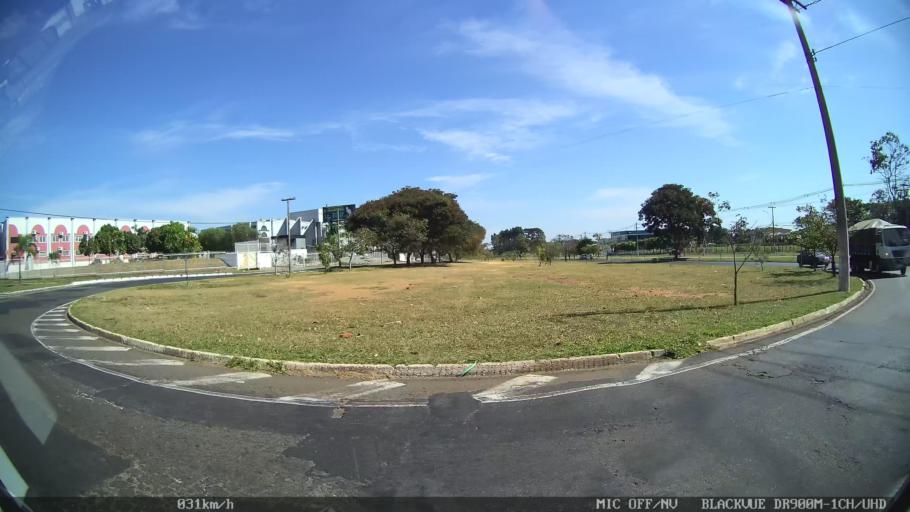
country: BR
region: Sao Paulo
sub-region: Franca
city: Franca
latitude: -20.5482
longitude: -47.4371
